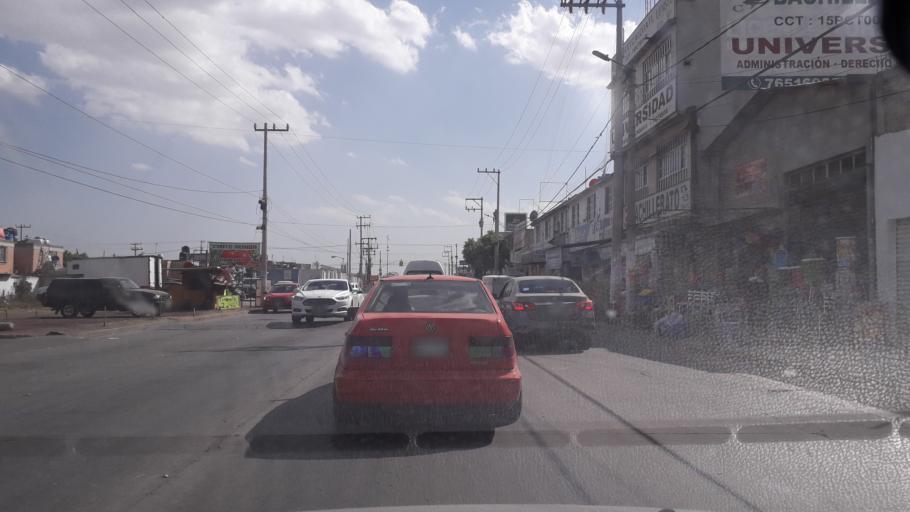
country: MX
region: Mexico
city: Ecatepec
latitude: 19.6254
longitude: -99.0489
